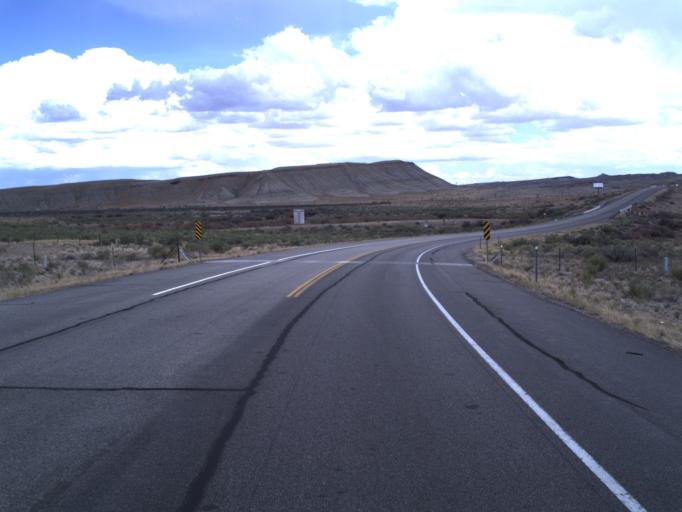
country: US
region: Utah
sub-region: Carbon County
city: East Carbon City
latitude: 38.9898
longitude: -110.1289
